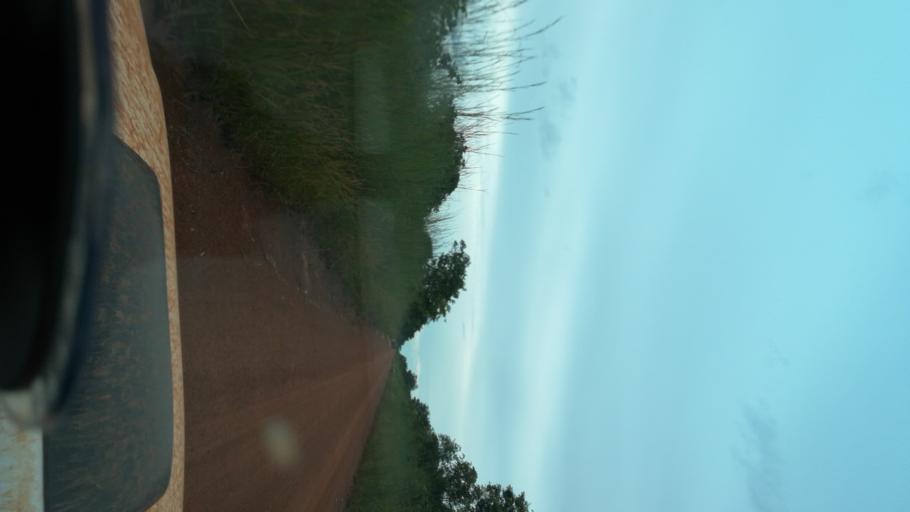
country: ZM
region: Luapula
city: Nchelenge
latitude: -9.3237
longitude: 28.2447
